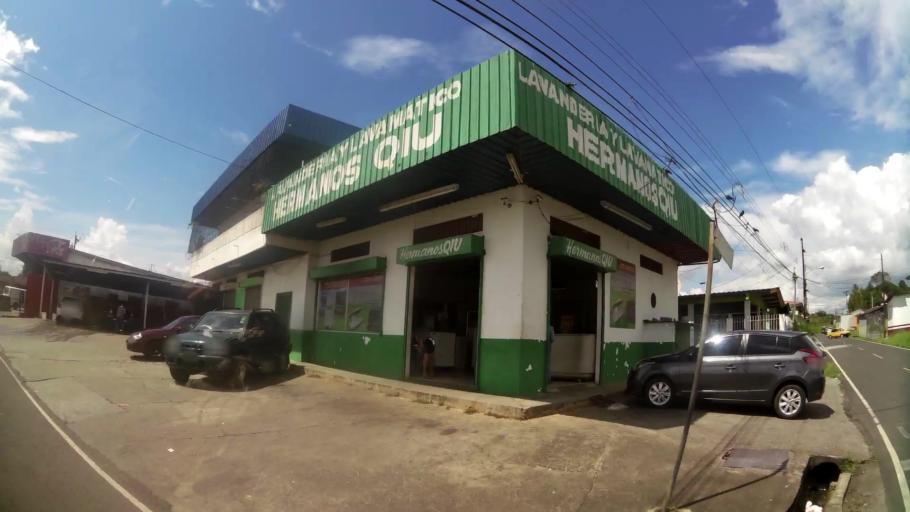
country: PA
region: Panama
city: San Vicente de Bique
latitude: 8.9190
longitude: -79.6973
